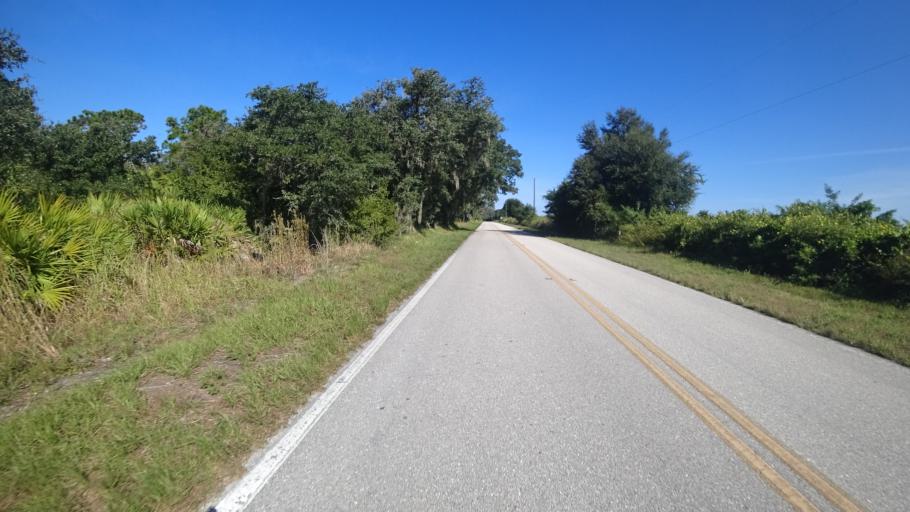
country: US
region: Florida
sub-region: Hillsborough County
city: Wimauma
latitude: 27.6381
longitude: -82.2924
